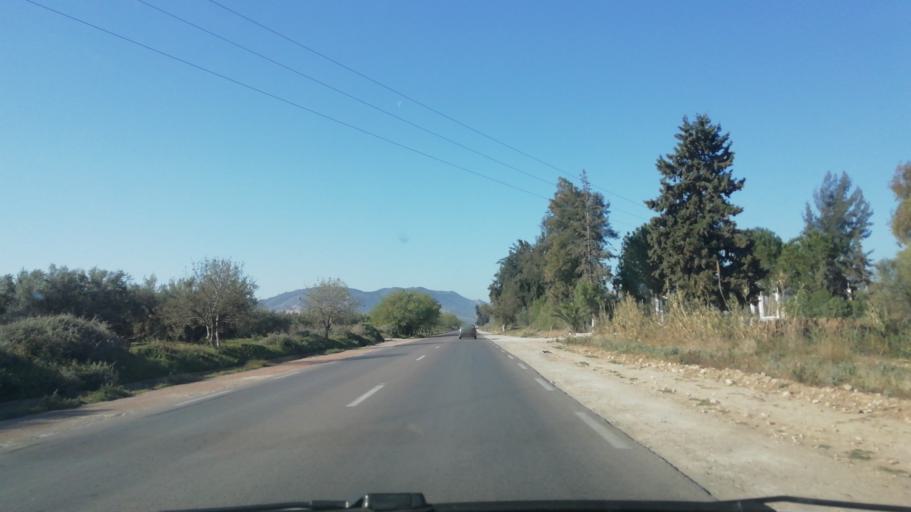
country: DZ
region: Mascara
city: Sig
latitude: 35.5446
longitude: -0.1237
